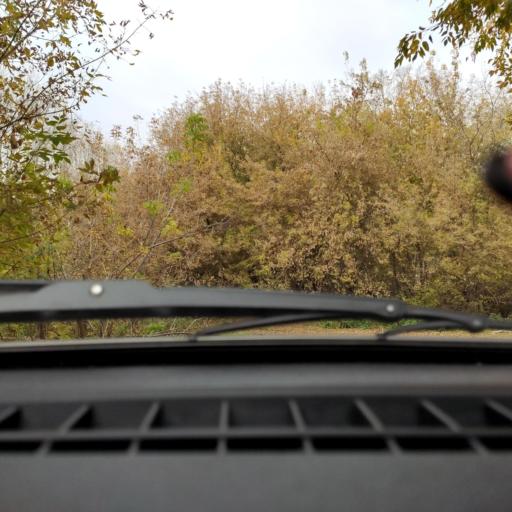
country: RU
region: Bashkortostan
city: Ufa
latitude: 54.7731
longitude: 56.1133
